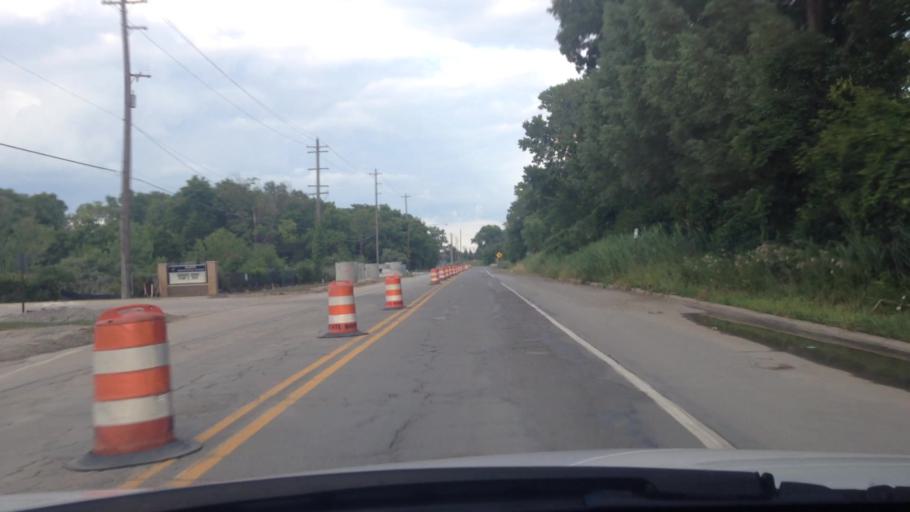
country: US
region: Michigan
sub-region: Wayne County
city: Woodhaven
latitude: 42.1684
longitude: -83.2542
